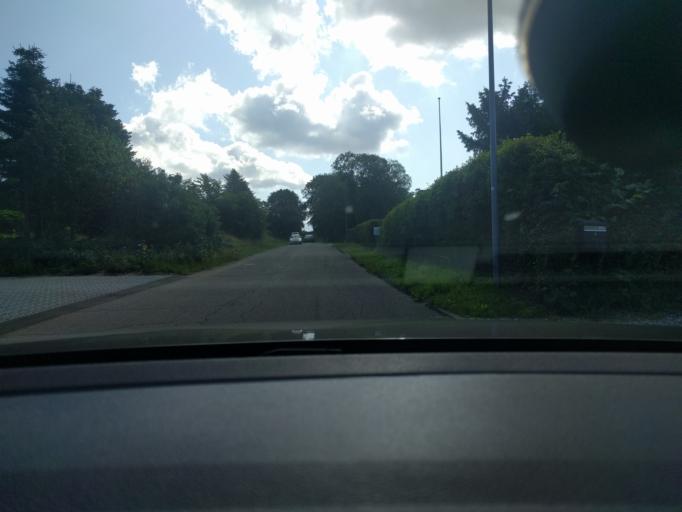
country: DK
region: Central Jutland
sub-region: Viborg Kommune
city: Viborg
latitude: 56.5296
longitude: 9.3221
